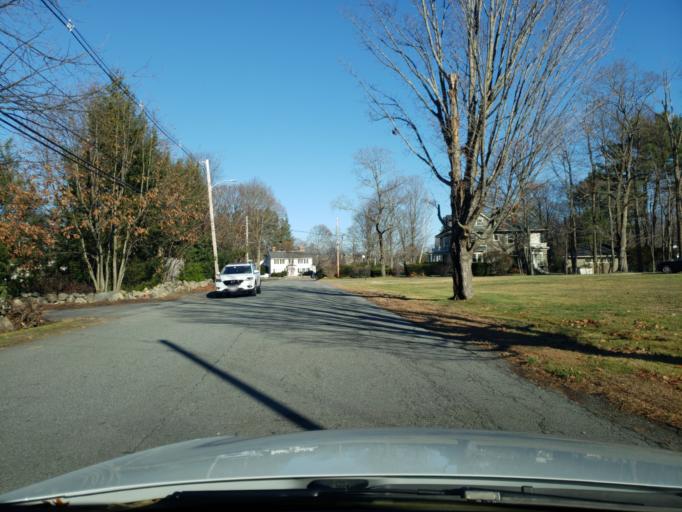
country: US
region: Massachusetts
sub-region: Essex County
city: Andover
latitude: 42.6403
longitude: -71.1331
